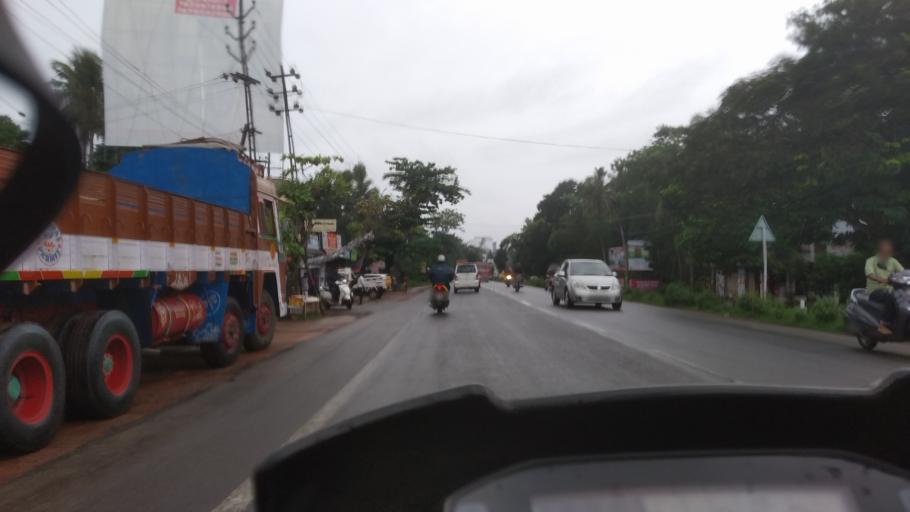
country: IN
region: Kerala
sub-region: Alappuzha
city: Kayankulam
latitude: 9.1271
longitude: 76.5163
